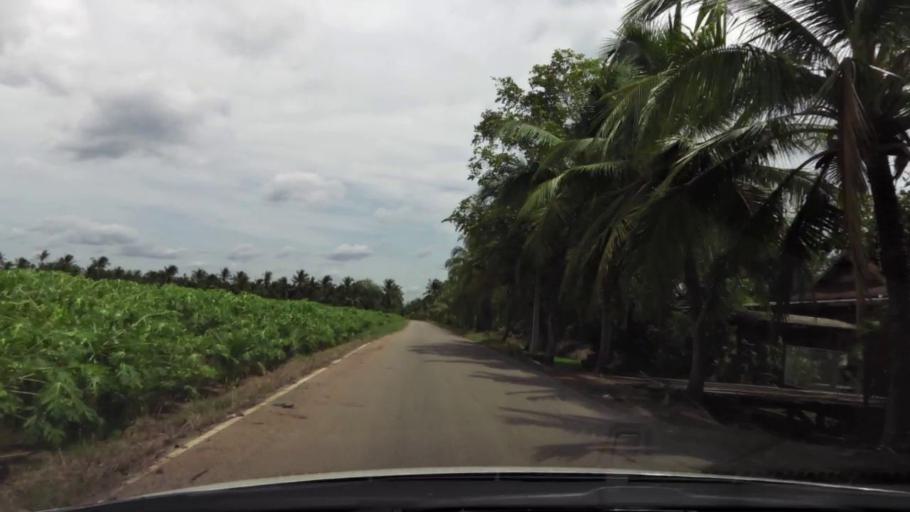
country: TH
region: Ratchaburi
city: Damnoen Saduak
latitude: 13.5320
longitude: 100.0012
